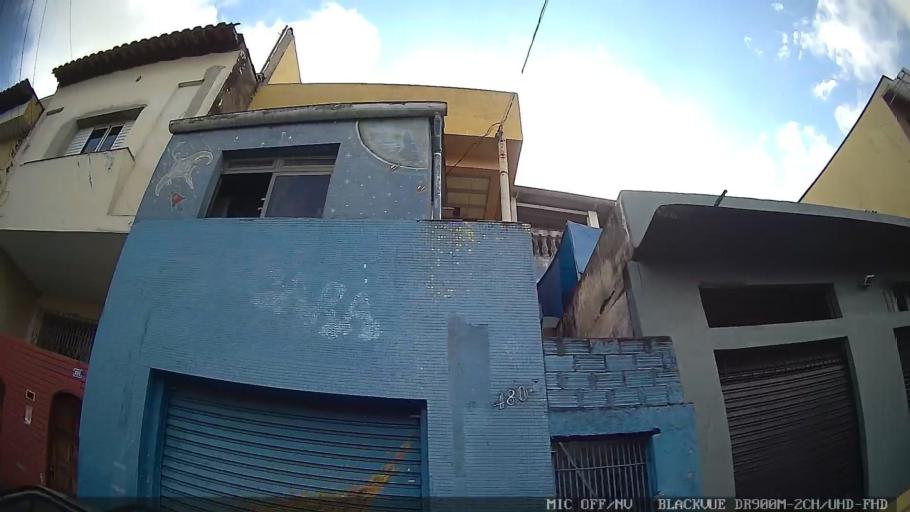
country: BR
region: Sao Paulo
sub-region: Sao Caetano Do Sul
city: Sao Caetano do Sul
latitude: -23.5659
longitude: -46.5368
